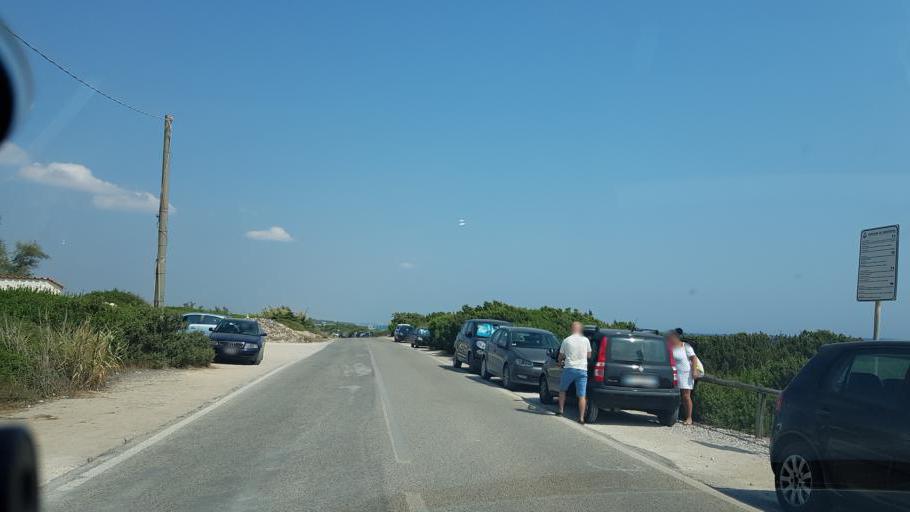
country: IT
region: Apulia
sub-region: Provincia di Taranto
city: Maruggio
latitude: 40.3018
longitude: 17.6170
